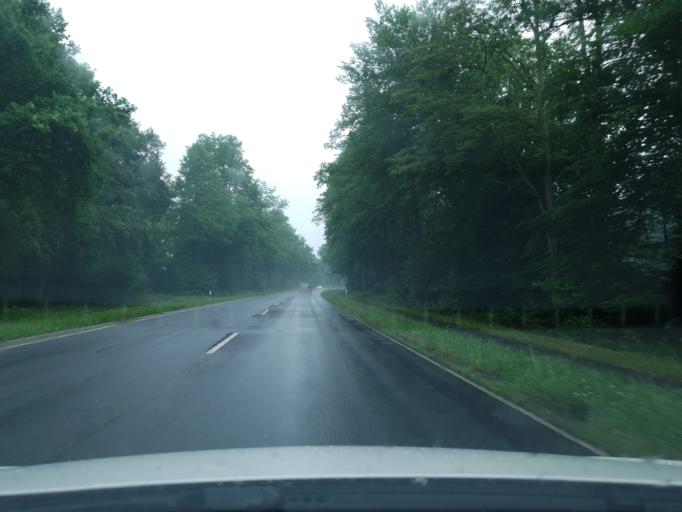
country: DE
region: Lower Saxony
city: Lingen
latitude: 52.5482
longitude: 7.2930
